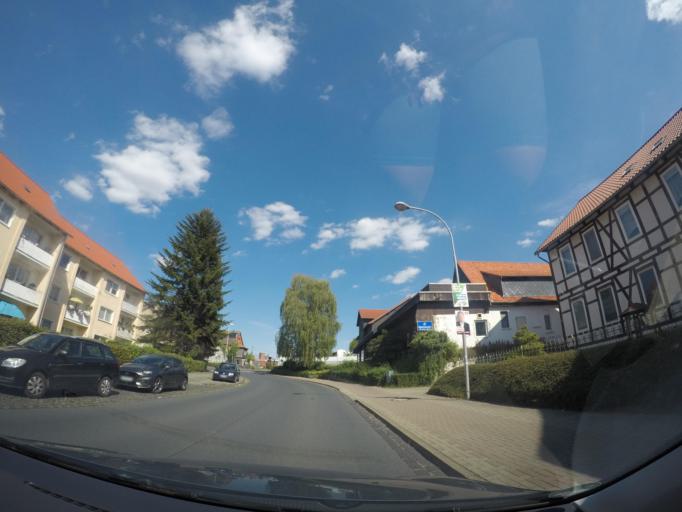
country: DE
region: Lower Saxony
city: Seesen
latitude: 51.8877
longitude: 10.1774
